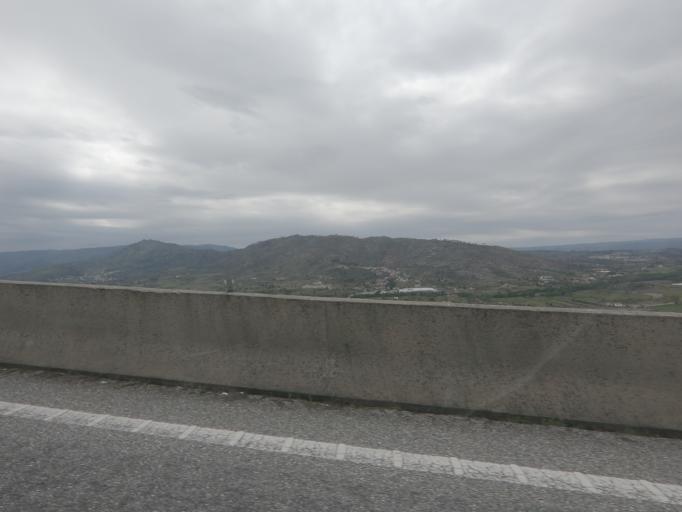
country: PT
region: Guarda
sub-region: Guarda
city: Guarda
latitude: 40.6079
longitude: -7.2829
